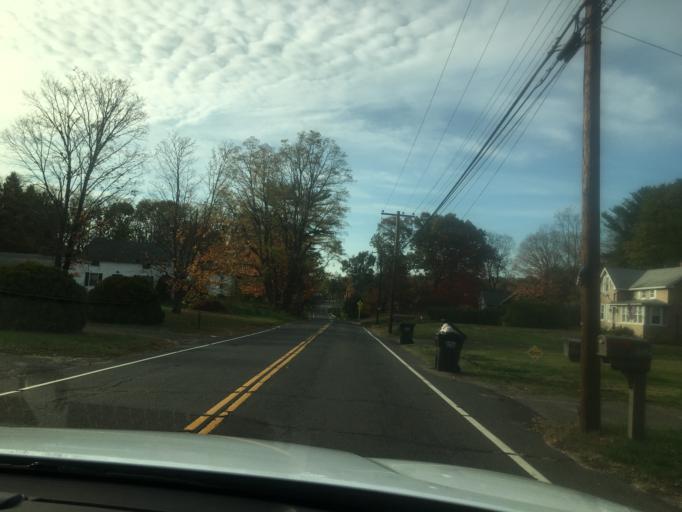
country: US
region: Connecticut
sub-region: Hartford County
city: South Windsor
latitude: 41.8147
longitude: -72.5957
